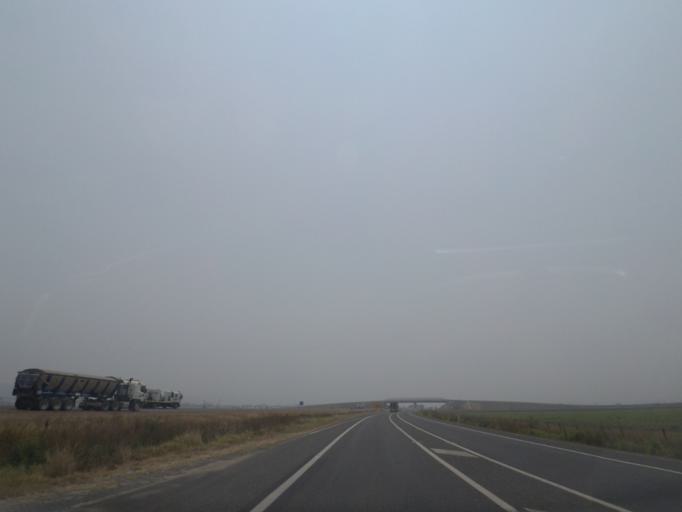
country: AU
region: New South Wales
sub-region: Clarence Valley
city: Maclean
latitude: -29.3966
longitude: 153.2393
